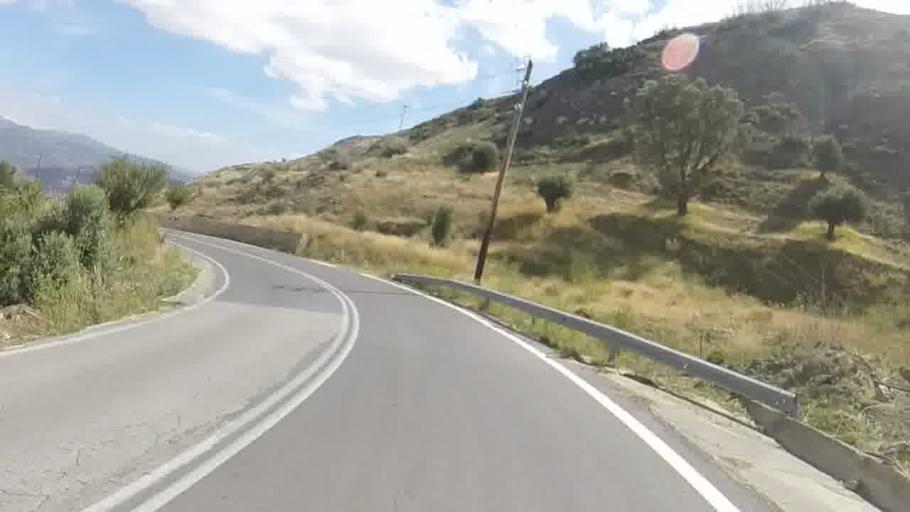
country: GR
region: Crete
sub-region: Nomos Rethymnis
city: Agia Galini
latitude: 35.1426
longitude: 24.6354
